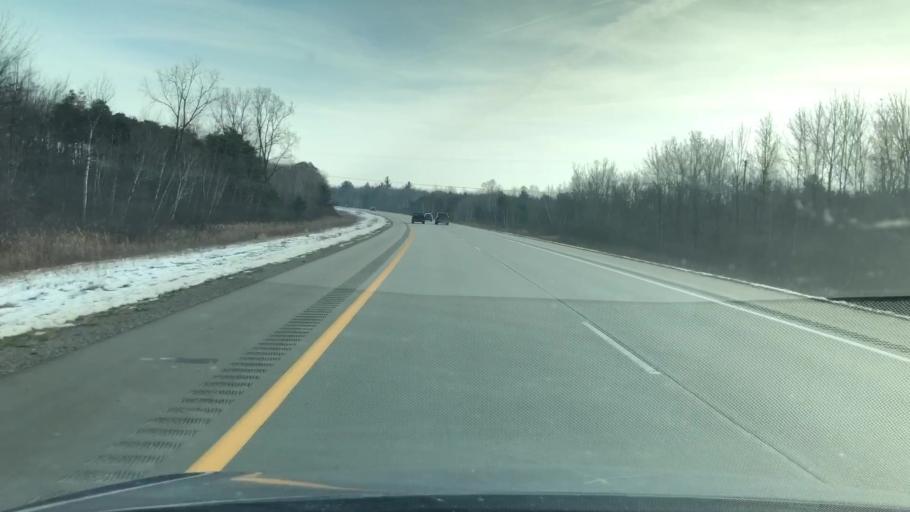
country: US
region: Michigan
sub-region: Arenac County
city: Standish
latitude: 44.0054
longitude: -84.0370
